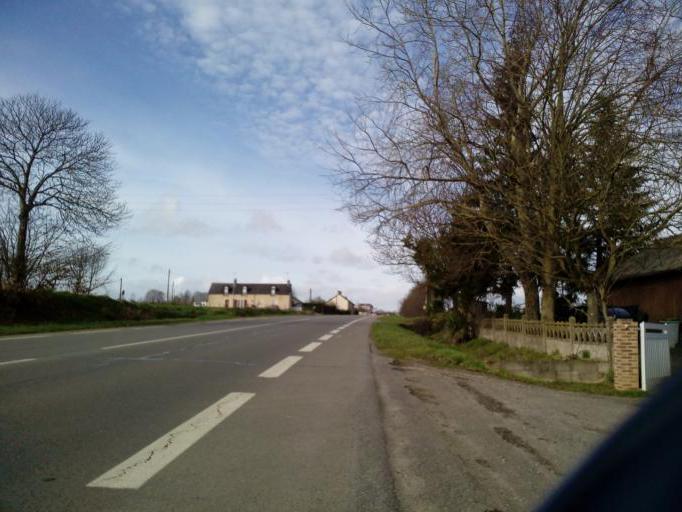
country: FR
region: Brittany
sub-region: Departement d'Ille-et-Vilaine
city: Montgermont
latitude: 48.1682
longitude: -1.7176
